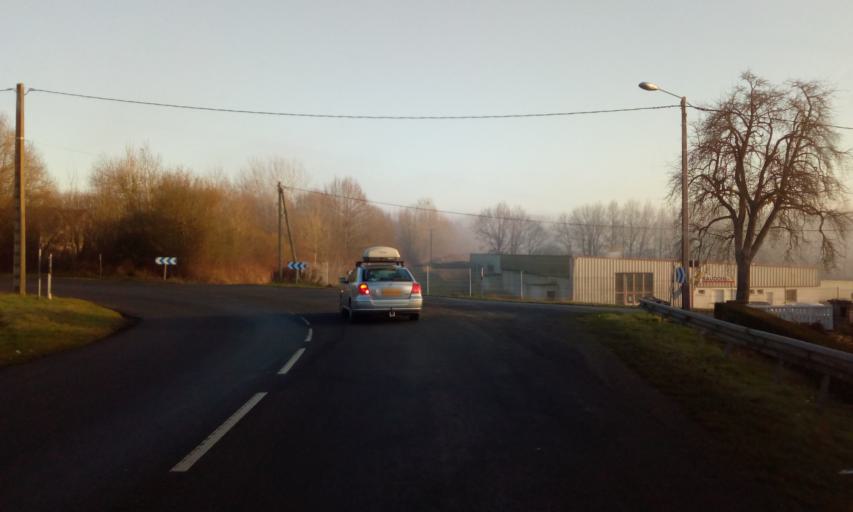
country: FR
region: Champagne-Ardenne
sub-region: Departement des Ardennes
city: Renwez
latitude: 49.8123
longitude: 4.5813
